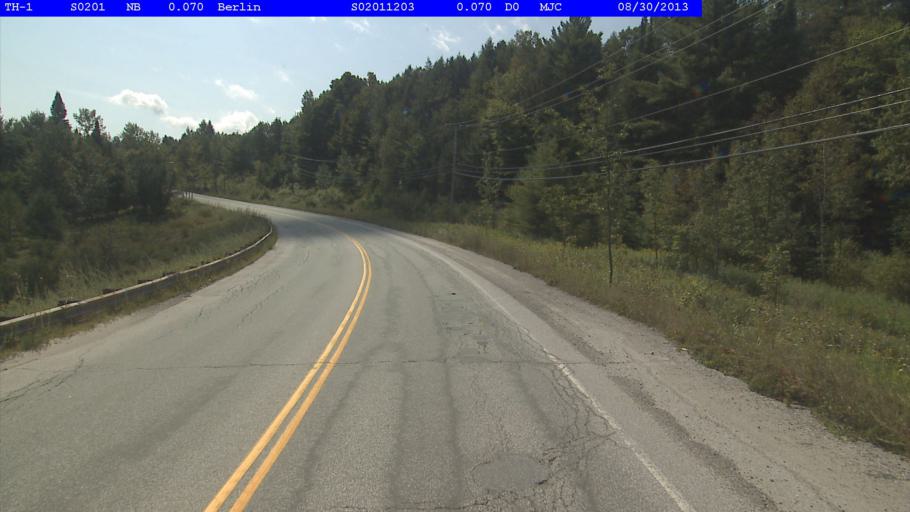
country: US
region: Vermont
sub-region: Washington County
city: Montpelier
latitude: 44.2367
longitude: -72.5651
